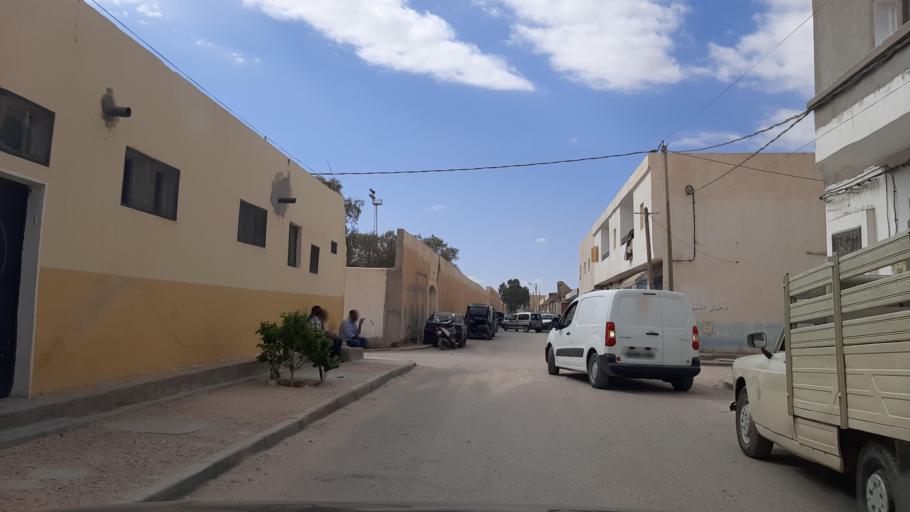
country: TN
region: Tataouine
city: Tataouine
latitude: 32.9289
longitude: 10.4432
